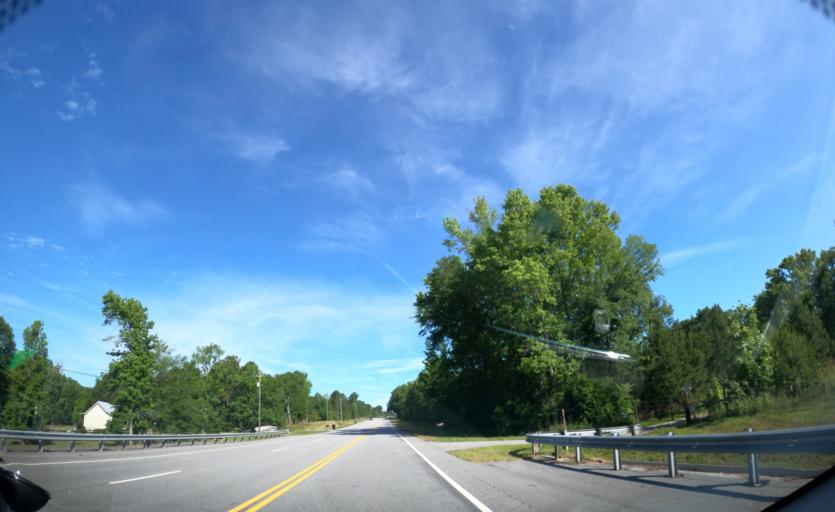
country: US
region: Georgia
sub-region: Columbia County
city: Appling
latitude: 33.6506
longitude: -82.3200
